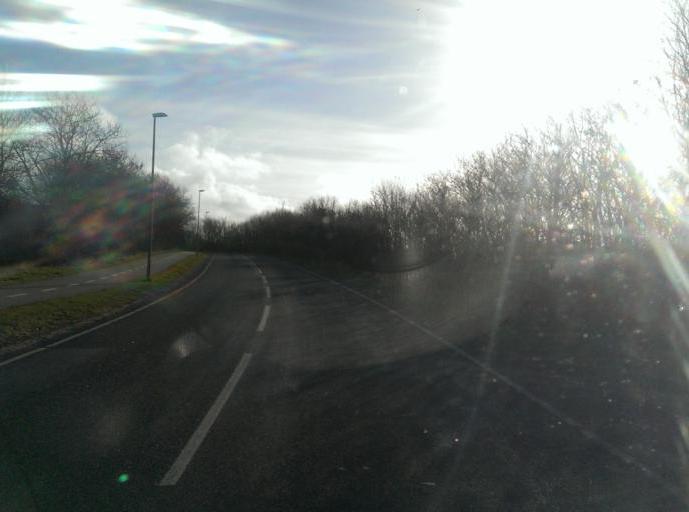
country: DK
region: South Denmark
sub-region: Esbjerg Kommune
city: Bramming
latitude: 55.4264
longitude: 8.6531
